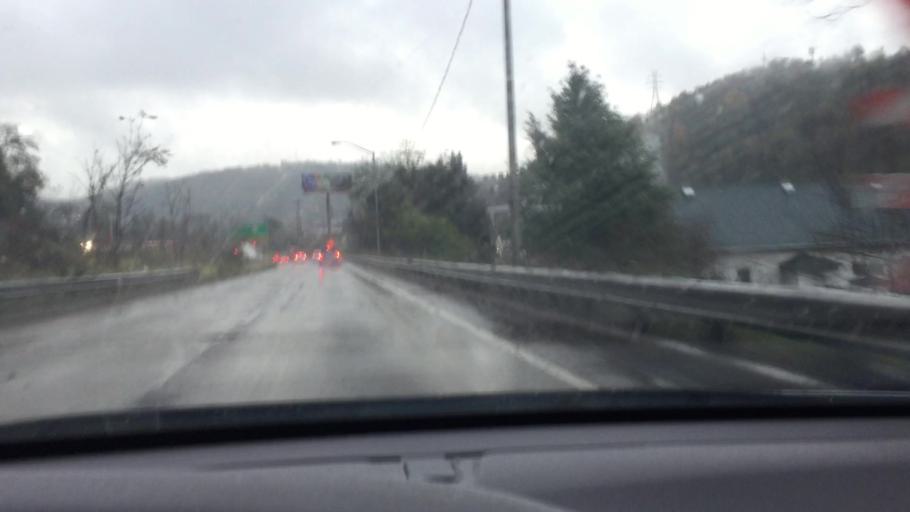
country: US
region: Pennsylvania
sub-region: Allegheny County
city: West Homestead
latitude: 40.3870
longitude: -79.9334
